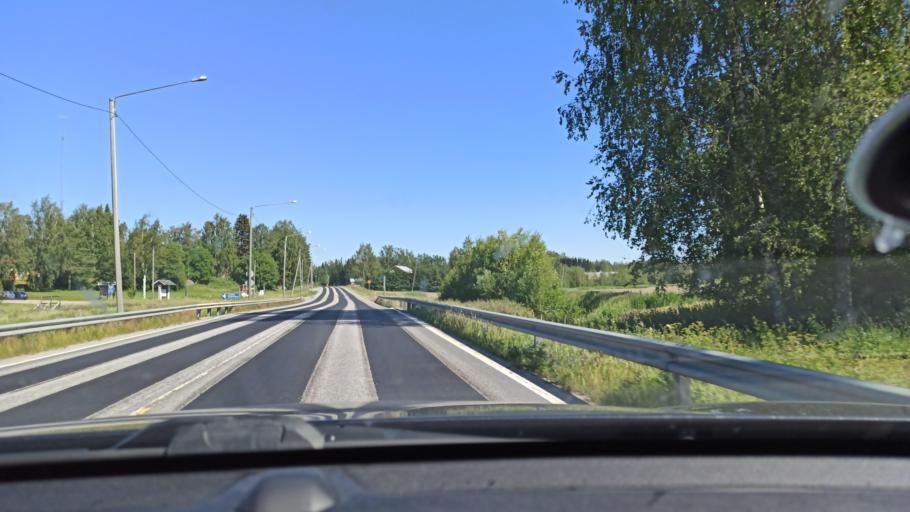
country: FI
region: Ostrobothnia
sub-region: Vaasa
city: Vaehaekyroe
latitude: 63.2024
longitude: 22.1074
